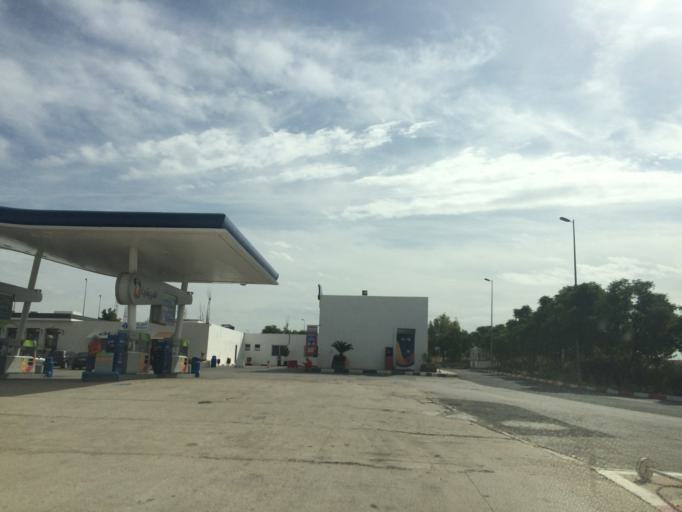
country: MA
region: Meknes-Tafilalet
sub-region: Meknes
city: Meknes
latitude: 33.8321
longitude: -5.5721
